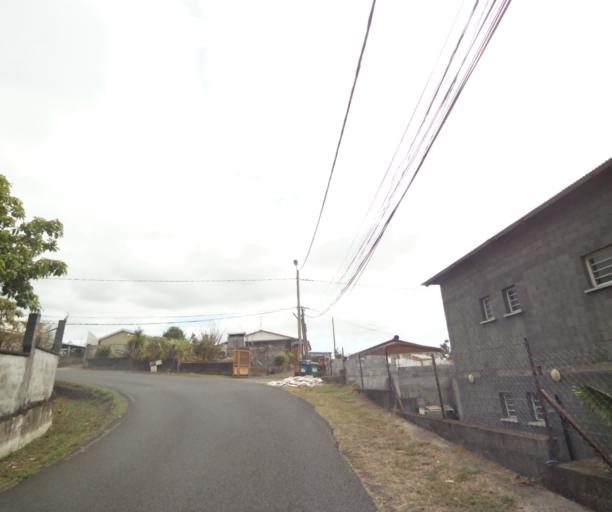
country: RE
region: Reunion
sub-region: Reunion
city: Saint-Paul
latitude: -21.0292
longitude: 55.3093
